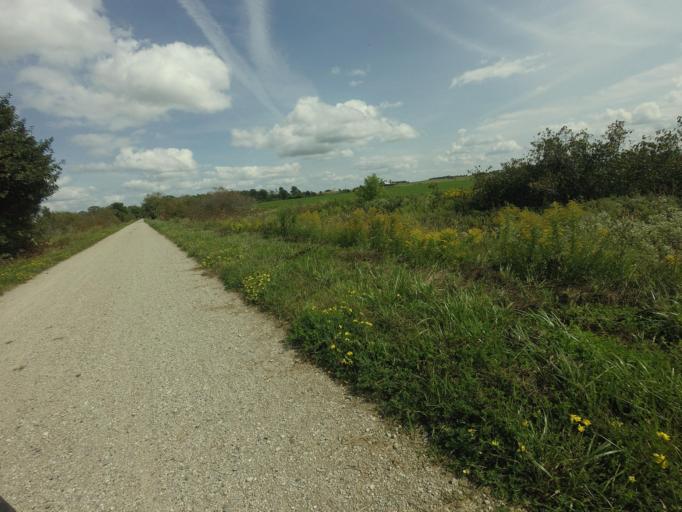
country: CA
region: Ontario
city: Waterloo
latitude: 43.5856
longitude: -80.7153
